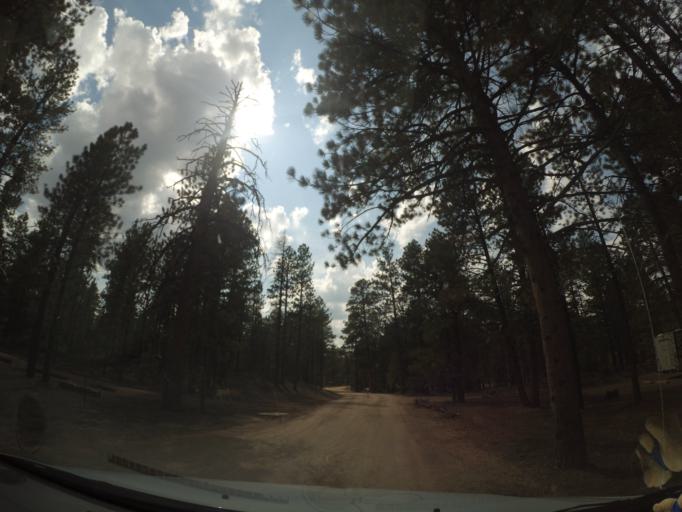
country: US
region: Utah
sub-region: Garfield County
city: Panguitch
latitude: 37.6227
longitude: -112.1737
